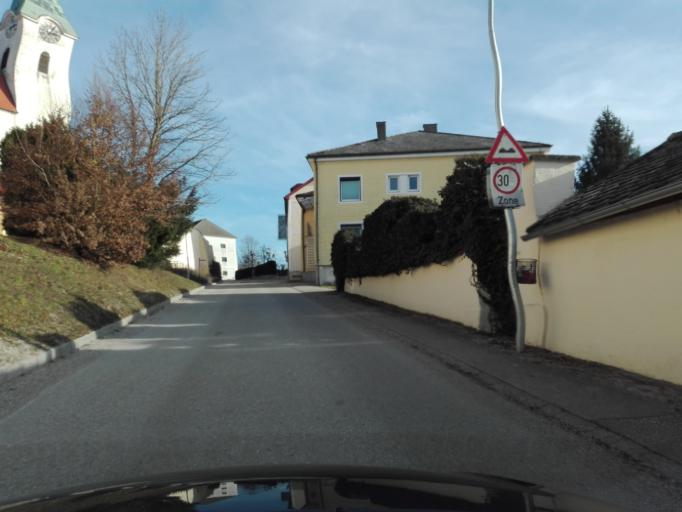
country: AT
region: Lower Austria
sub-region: Politischer Bezirk Amstetten
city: Amstetten
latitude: 48.1612
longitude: 14.8439
